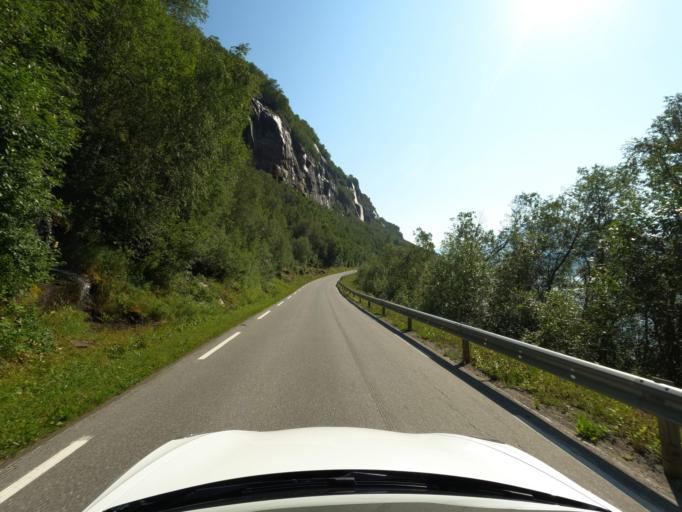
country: NO
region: Nordland
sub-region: Narvik
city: Narvik
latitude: 68.3510
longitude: 17.2785
